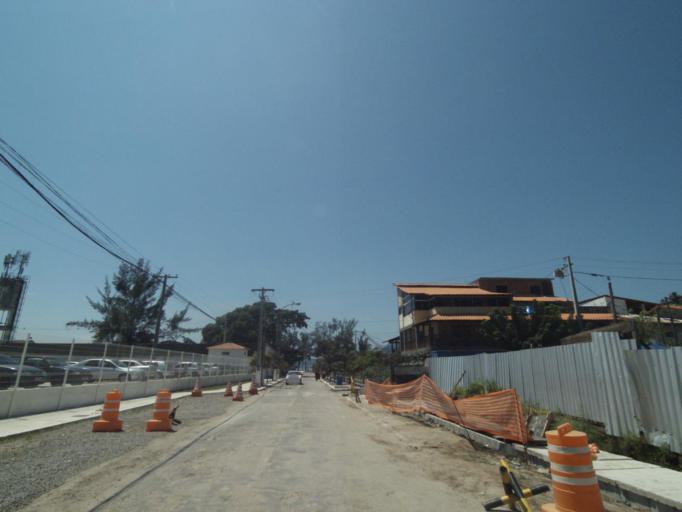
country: BR
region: Rio de Janeiro
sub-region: Niteroi
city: Niteroi
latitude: -22.9356
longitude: -43.1145
